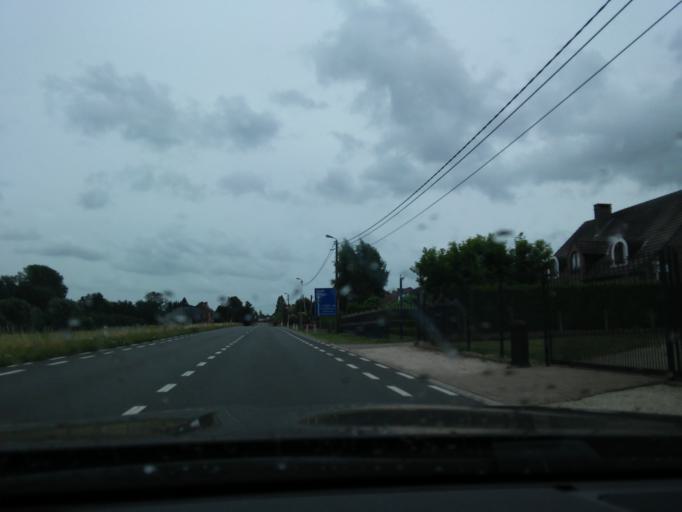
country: BE
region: Flanders
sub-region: Provincie Vlaams-Brabant
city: Herne
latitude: 50.7057
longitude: 4.0295
